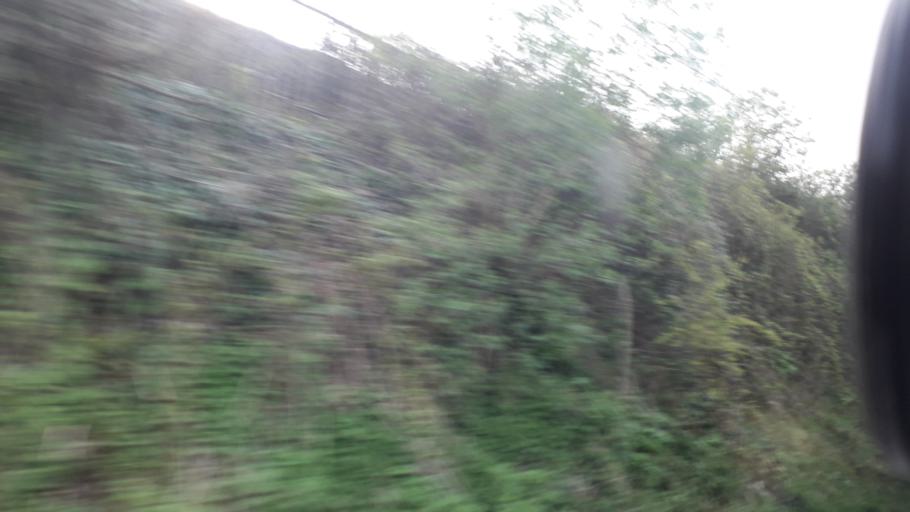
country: IE
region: Leinster
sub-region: Kildare
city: Kilcock
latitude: 53.4019
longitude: -6.6748
